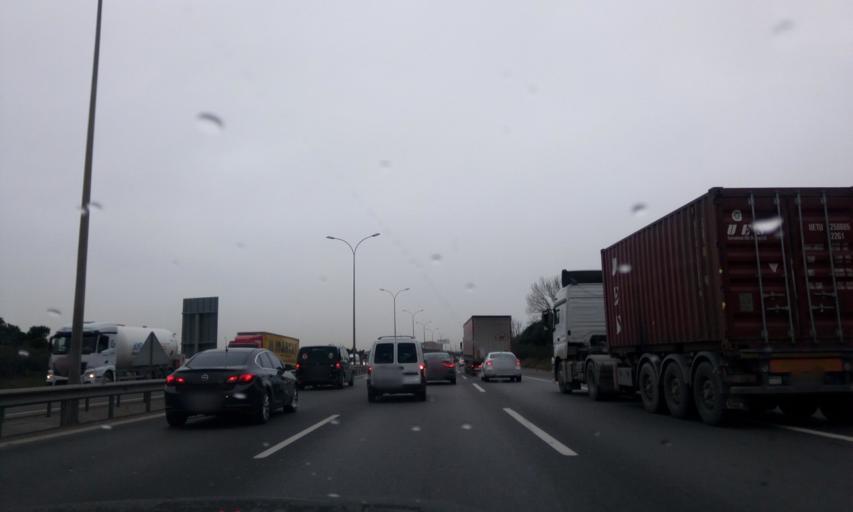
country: TR
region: Kocaeli
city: Balcik
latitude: 40.8609
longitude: 29.4034
